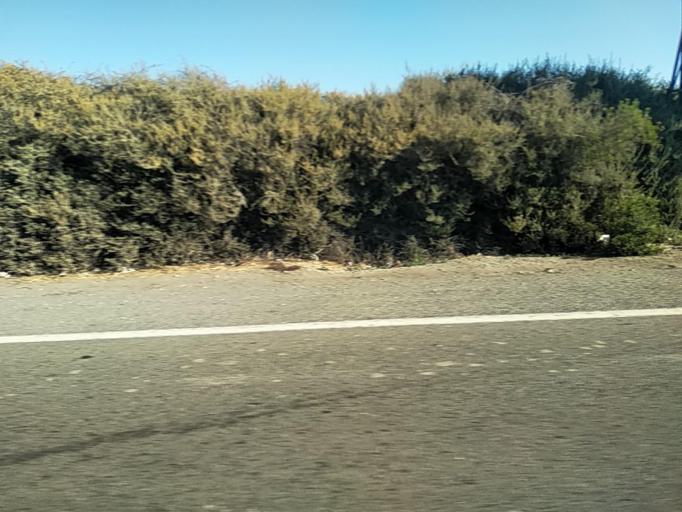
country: CL
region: Atacama
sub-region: Provincia de Copiapo
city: Copiapo
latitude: -27.2970
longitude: -70.4776
